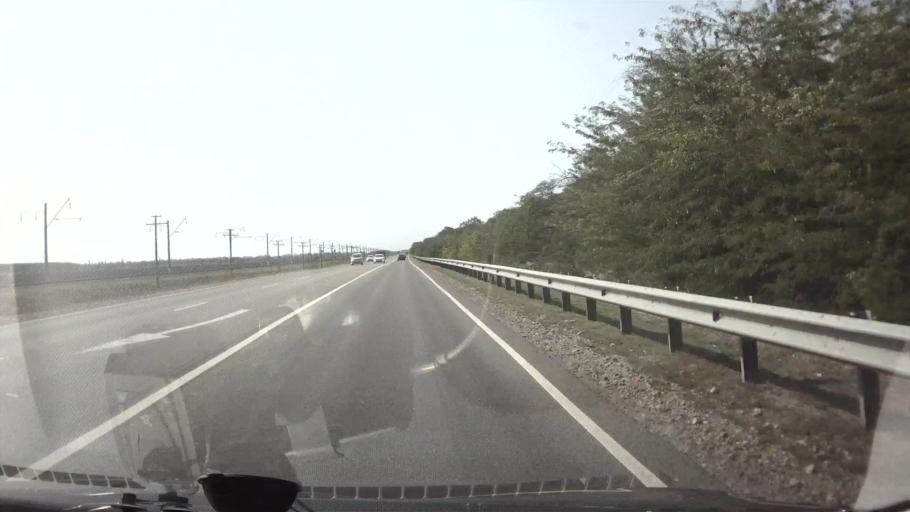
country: RU
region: Krasnodarskiy
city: Dvubratskiy
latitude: 45.2841
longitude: 39.8490
